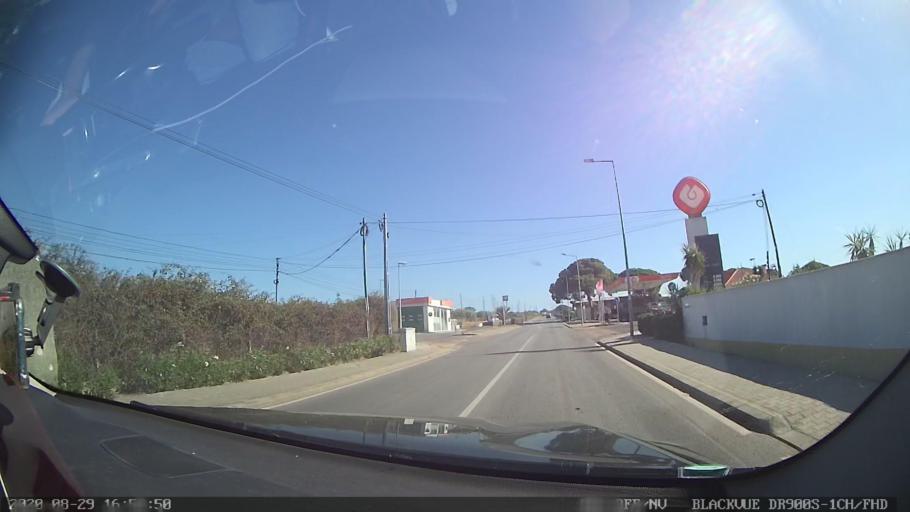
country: PT
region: Setubal
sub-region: Alcacer do Sal
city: Alcacer do Sal
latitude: 38.3929
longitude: -8.5138
